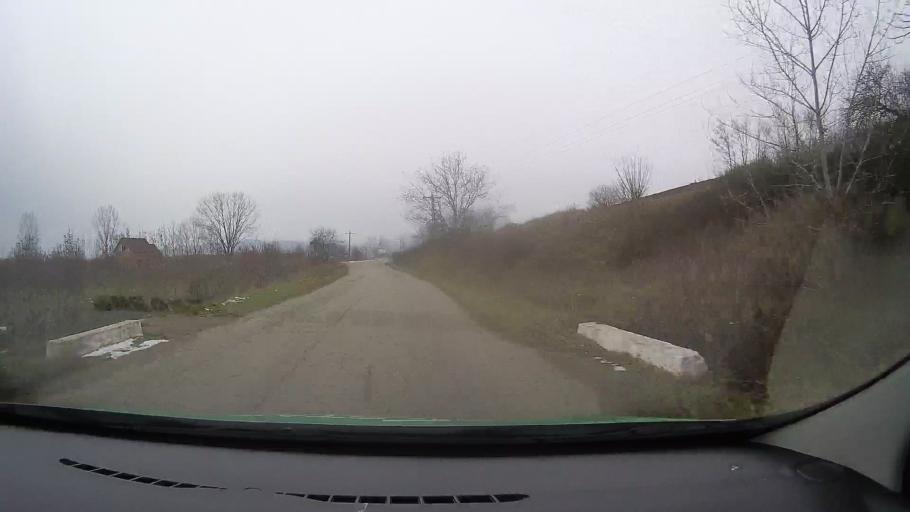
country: RO
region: Hunedoara
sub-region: Comuna Romos
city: Romos
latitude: 45.8659
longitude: 23.2728
